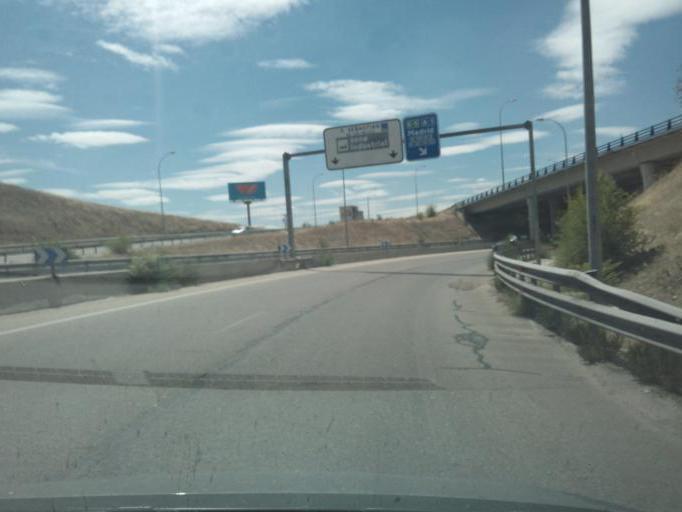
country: ES
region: Madrid
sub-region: Provincia de Madrid
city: San Sebastian de los Reyes
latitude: 40.5795
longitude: -3.5846
